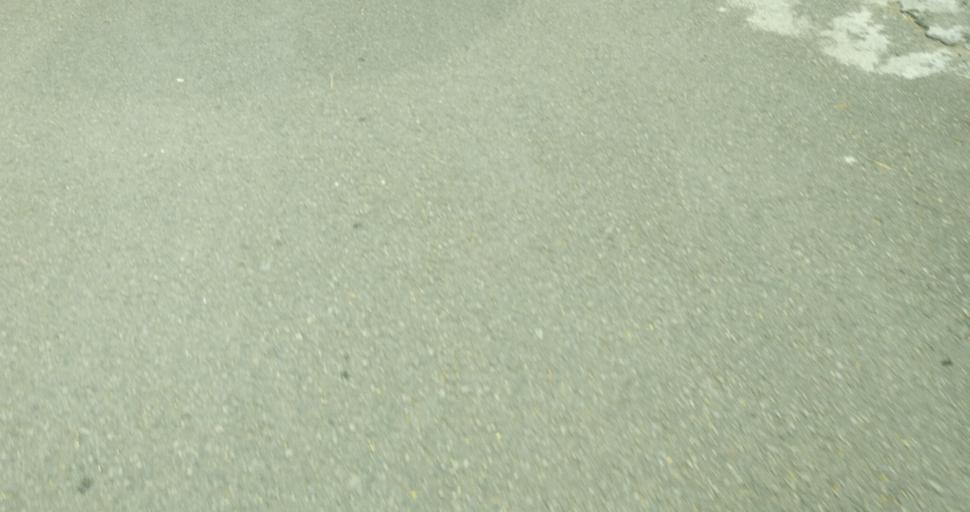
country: TW
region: Taiwan
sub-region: Hsinchu
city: Hsinchu
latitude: 24.7593
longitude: 120.9530
